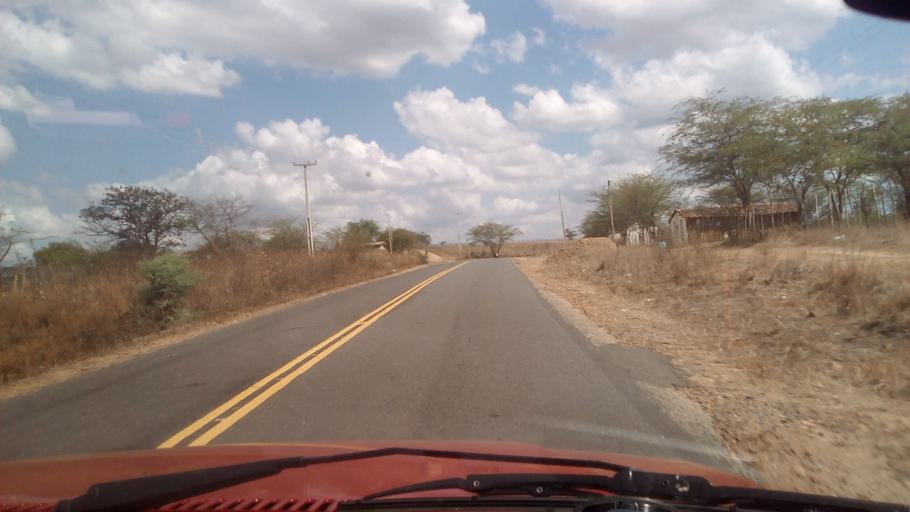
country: BR
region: Paraiba
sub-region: Cacimba De Dentro
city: Cacimba de Dentro
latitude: -6.7108
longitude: -35.7230
